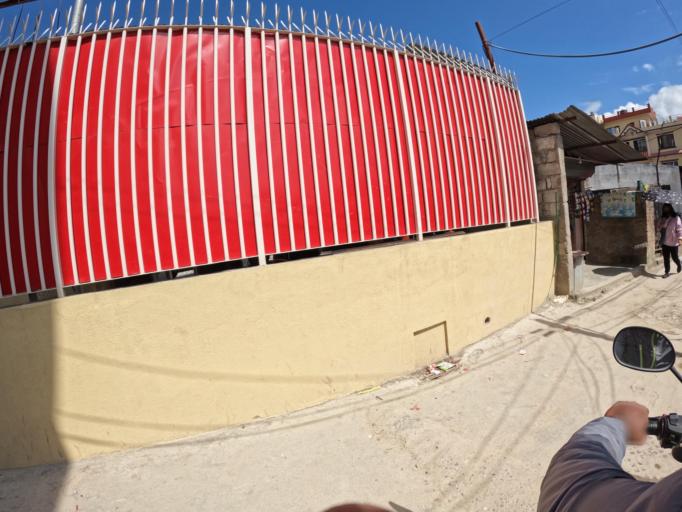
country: NP
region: Central Region
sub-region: Bagmati Zone
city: Kathmandu
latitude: 27.7448
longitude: 85.3332
